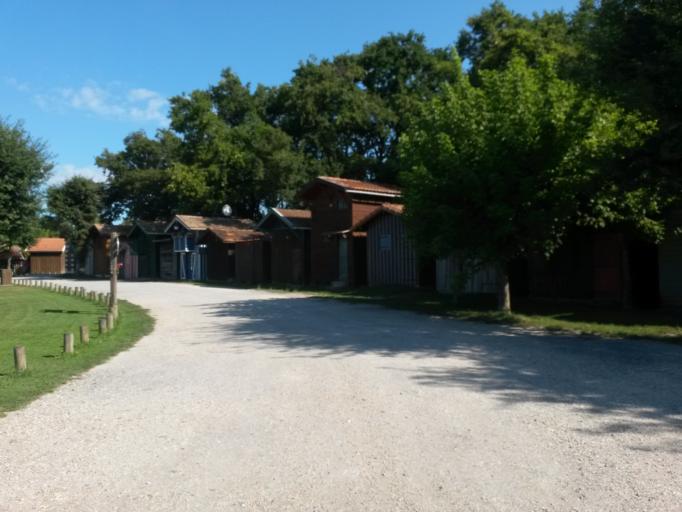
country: FR
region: Aquitaine
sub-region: Departement de la Gironde
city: Biganos
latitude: 44.6424
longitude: -0.9979
